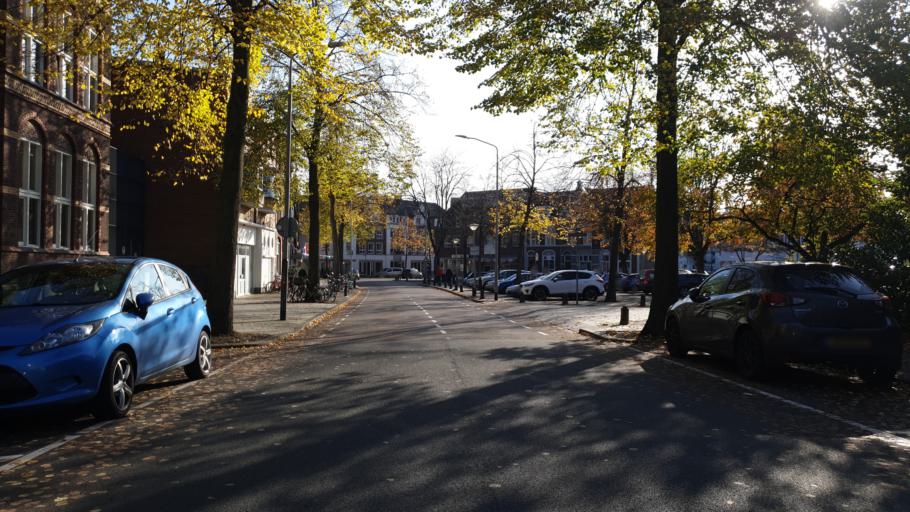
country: NL
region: Limburg
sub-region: Gemeente Venlo
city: Venlo
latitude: 51.3744
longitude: 6.1731
